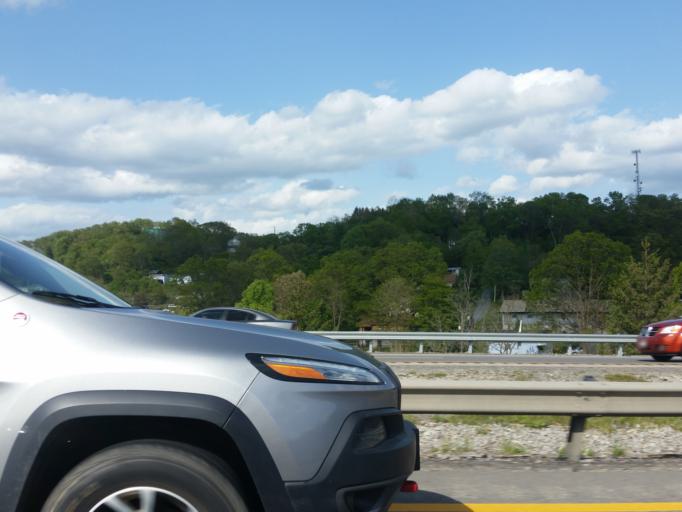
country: US
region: West Virginia
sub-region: Raleigh County
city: MacArthur
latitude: 37.7567
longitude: -81.2119
